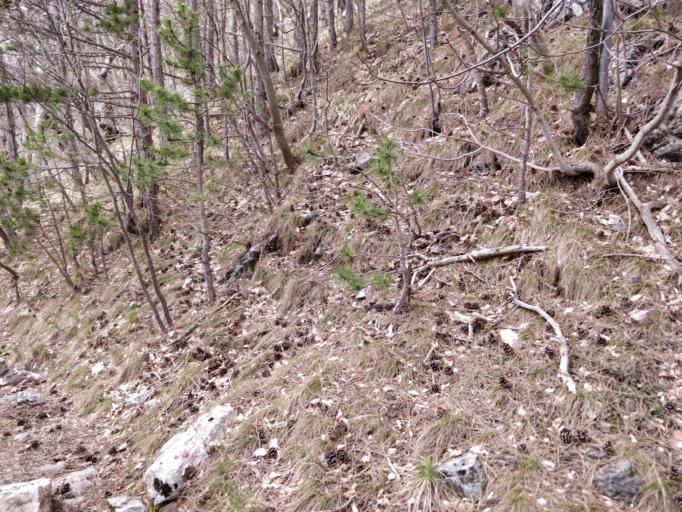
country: HR
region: Zadarska
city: Starigrad
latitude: 44.3289
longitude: 15.5218
